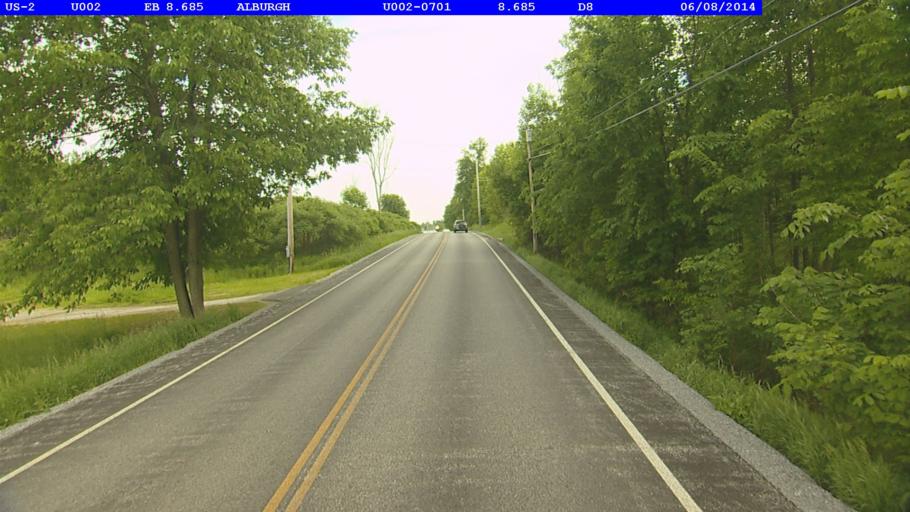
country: US
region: Vermont
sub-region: Grand Isle County
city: North Hero
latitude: 44.9255
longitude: -73.2743
